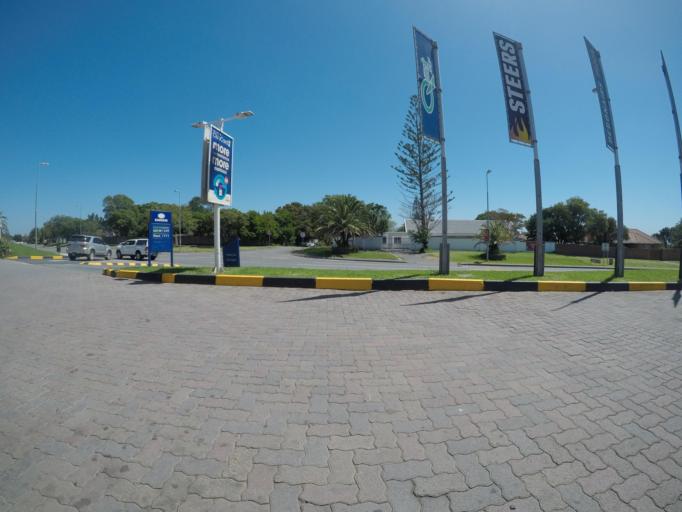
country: ZA
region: Eastern Cape
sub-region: Buffalo City Metropolitan Municipality
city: East London
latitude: -32.9665
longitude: 27.9385
